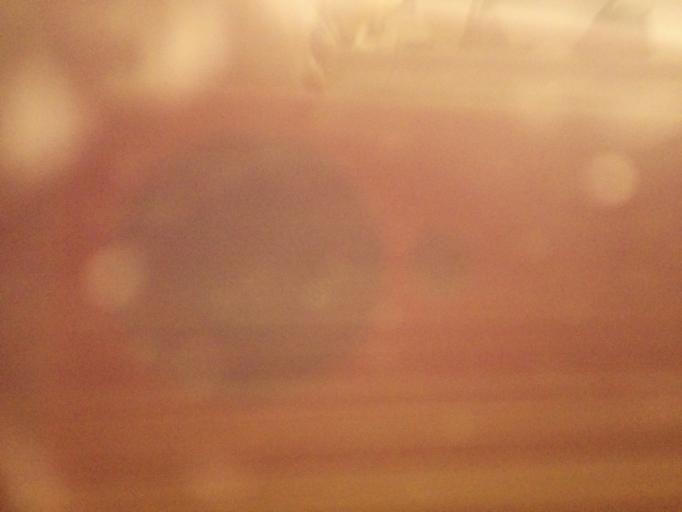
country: JP
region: Shizuoka
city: Fujinomiya
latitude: 35.1029
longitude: 138.5499
